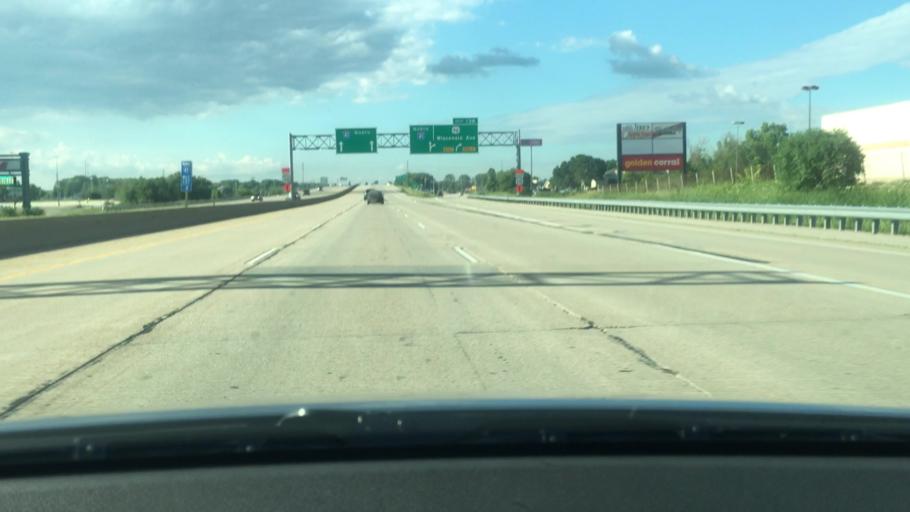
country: US
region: Wisconsin
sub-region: Outagamie County
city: Appleton
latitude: 44.2685
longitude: -88.4662
